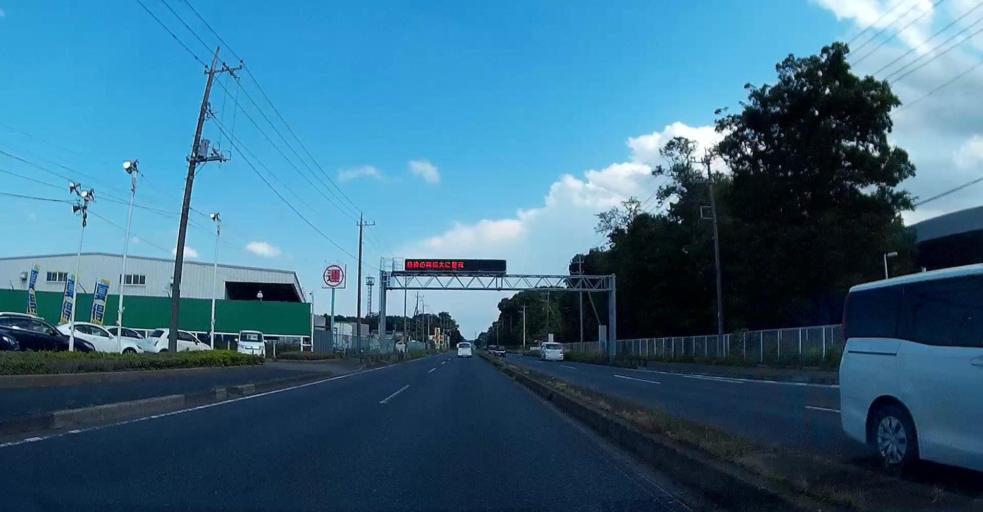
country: JP
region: Chiba
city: Noda
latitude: 35.9894
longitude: 139.8529
